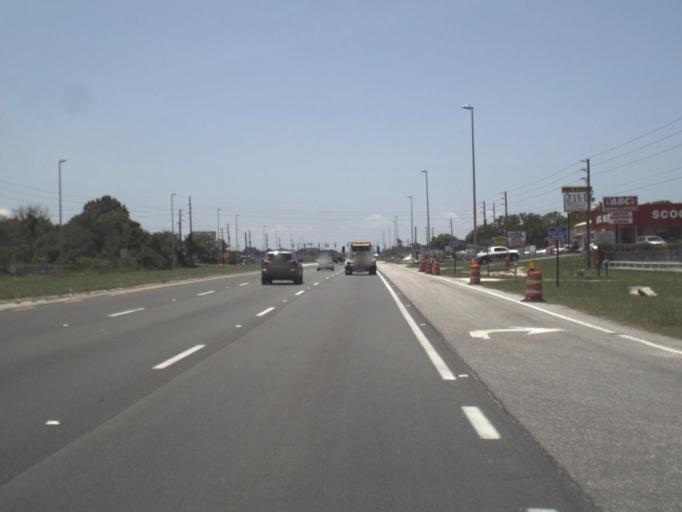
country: US
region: Florida
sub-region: Pasco County
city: Hudson
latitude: 28.3775
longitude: -82.6808
